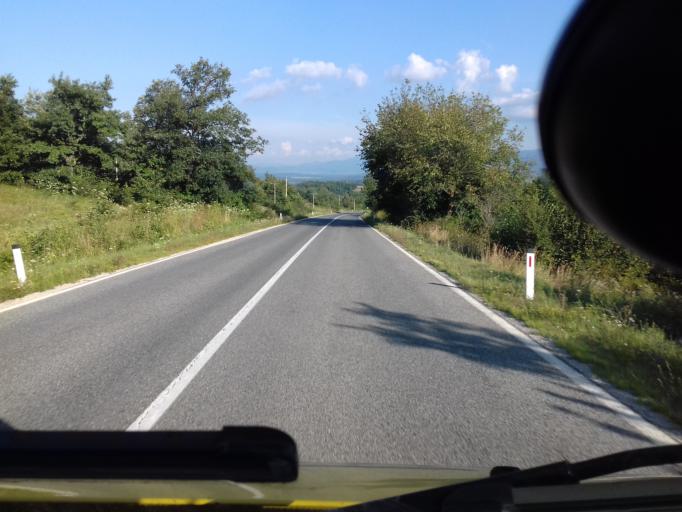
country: BA
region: Federation of Bosnia and Herzegovina
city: Orasac
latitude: 44.6521
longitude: 16.1590
